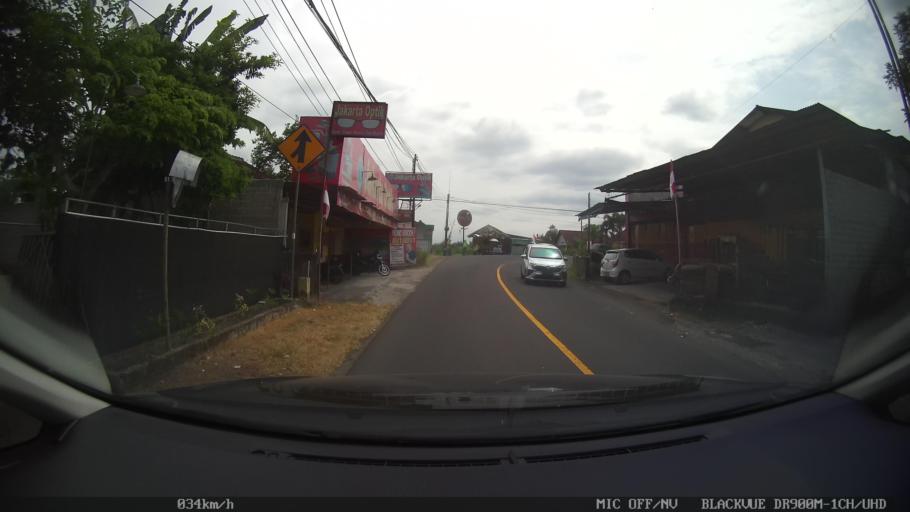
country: ID
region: Central Java
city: Candi Prambanan
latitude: -7.7364
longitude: 110.4793
